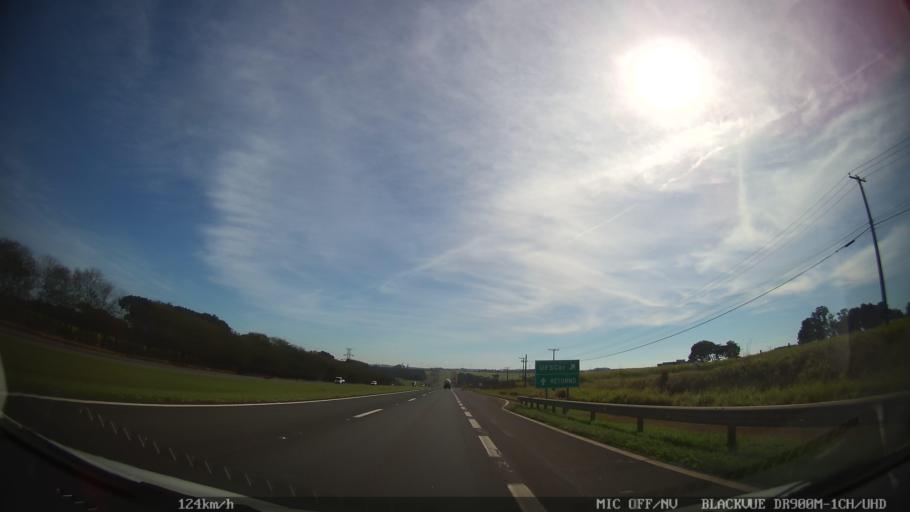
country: BR
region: Sao Paulo
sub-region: Araras
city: Araras
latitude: -22.3175
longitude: -47.3903
